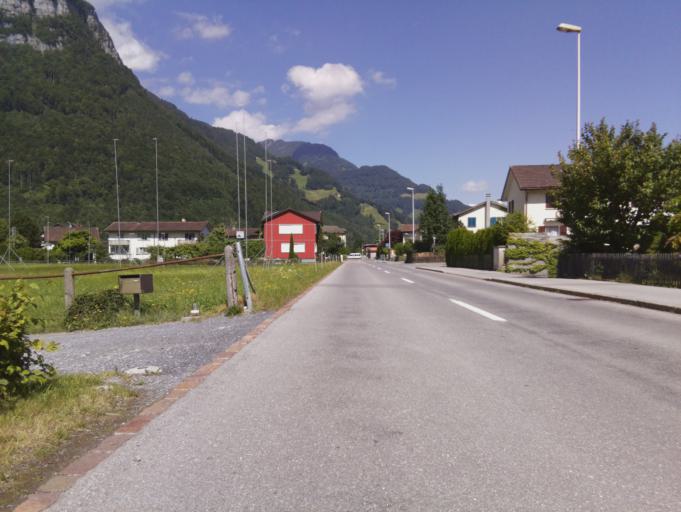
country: CH
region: Glarus
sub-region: Glarus
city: Nafels
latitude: 47.1036
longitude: 9.0673
